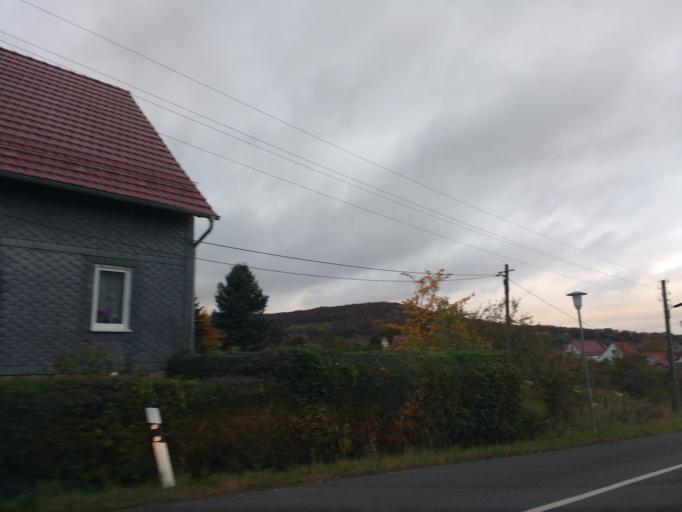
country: DE
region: Thuringia
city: Buhla
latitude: 51.4422
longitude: 10.4431
